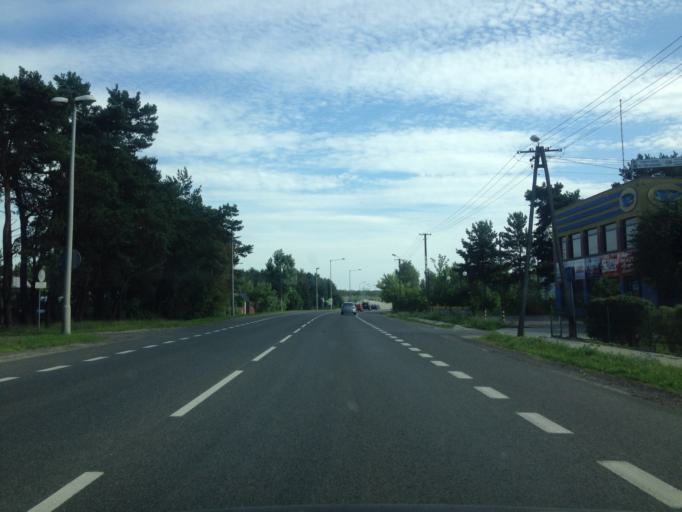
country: PL
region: Kujawsko-Pomorskie
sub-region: Torun
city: Torun
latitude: 52.9741
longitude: 18.6775
